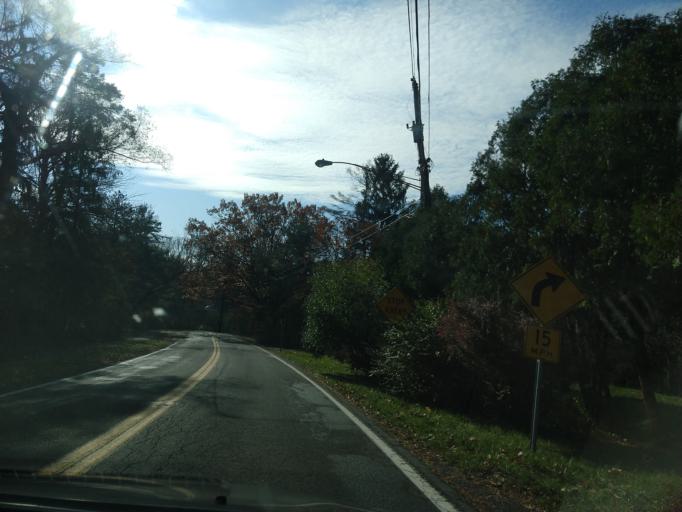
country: US
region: New York
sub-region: Tompkins County
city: Cayuga Heights
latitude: 42.4660
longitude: -76.4826
